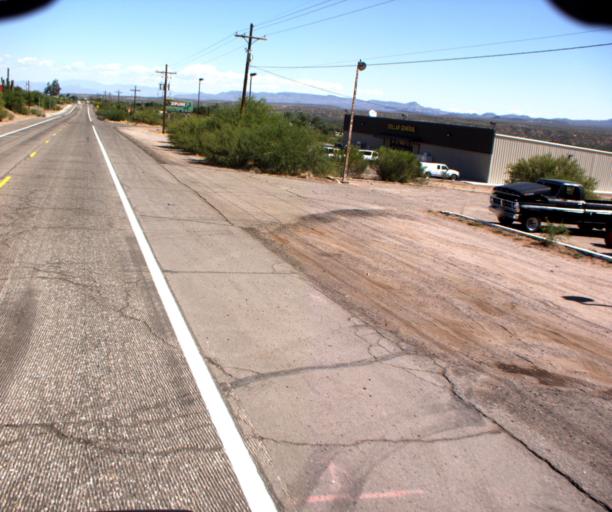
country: US
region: Arizona
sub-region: Pinal County
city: Mammoth
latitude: 32.7249
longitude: -110.6455
